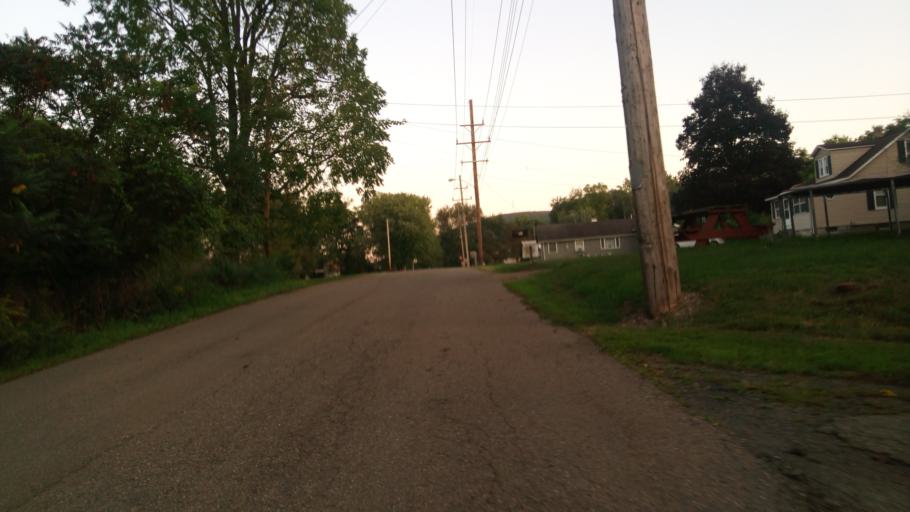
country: US
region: New York
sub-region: Chemung County
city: Elmira
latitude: 42.0651
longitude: -76.7908
